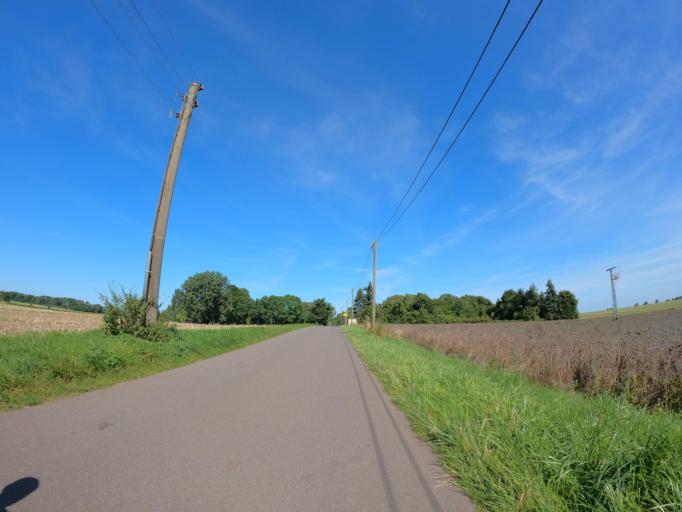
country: DE
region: Mecklenburg-Vorpommern
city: Kramerhof
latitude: 54.3716
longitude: 13.0487
